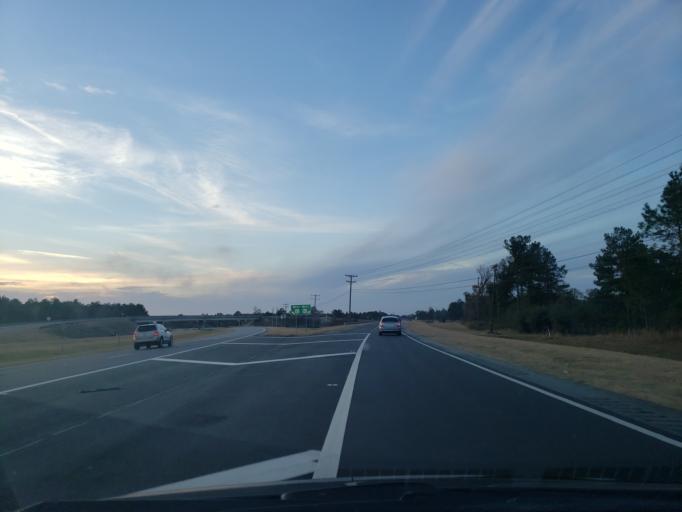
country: US
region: Georgia
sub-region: Dougherty County
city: Albany
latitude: 31.5724
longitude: -84.0267
